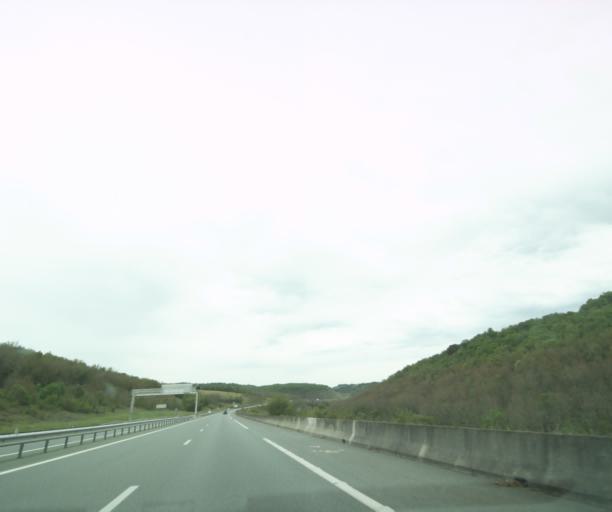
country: FR
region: Midi-Pyrenees
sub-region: Departement du Lot
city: Le Vigan
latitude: 44.7225
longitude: 1.5620
